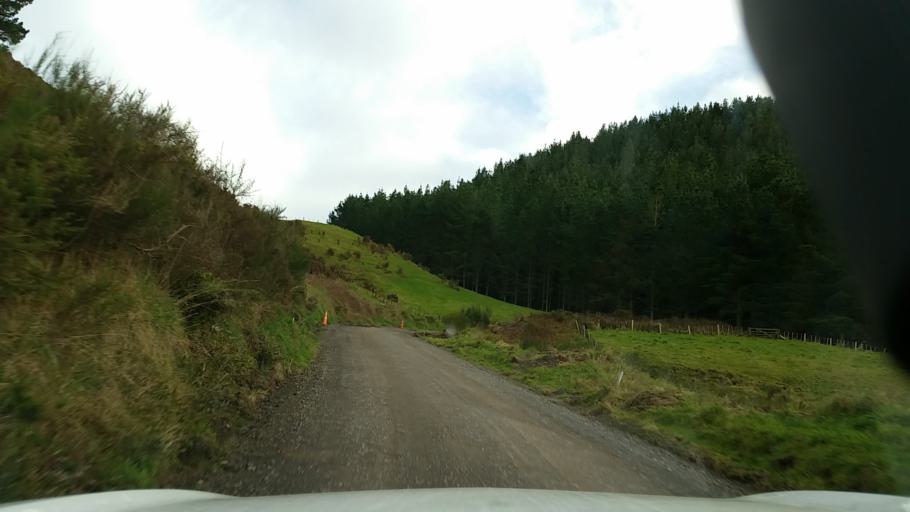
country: NZ
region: Bay of Plenty
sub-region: Rotorua District
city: Rotorua
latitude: -38.2248
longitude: 176.1611
